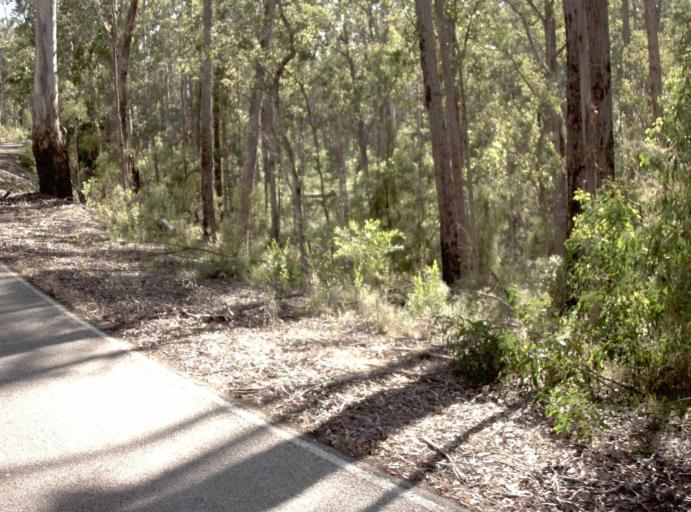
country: AU
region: Victoria
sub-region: East Gippsland
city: Lakes Entrance
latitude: -37.5589
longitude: 148.5549
